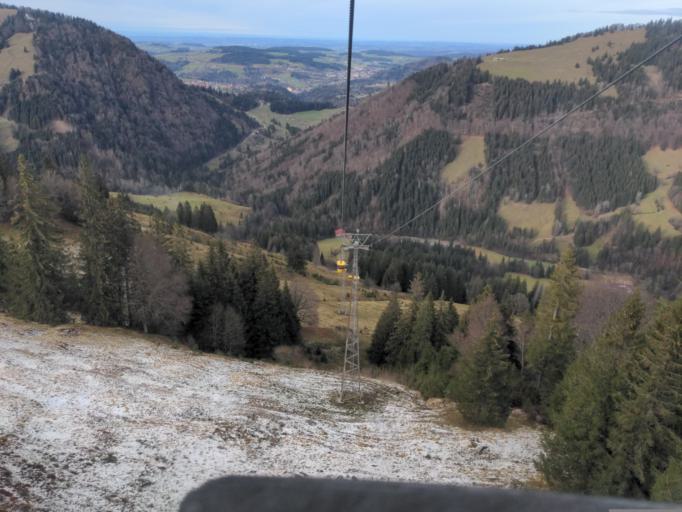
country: DE
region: Bavaria
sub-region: Swabia
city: Balderschwang
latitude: 47.5010
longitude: 10.0652
